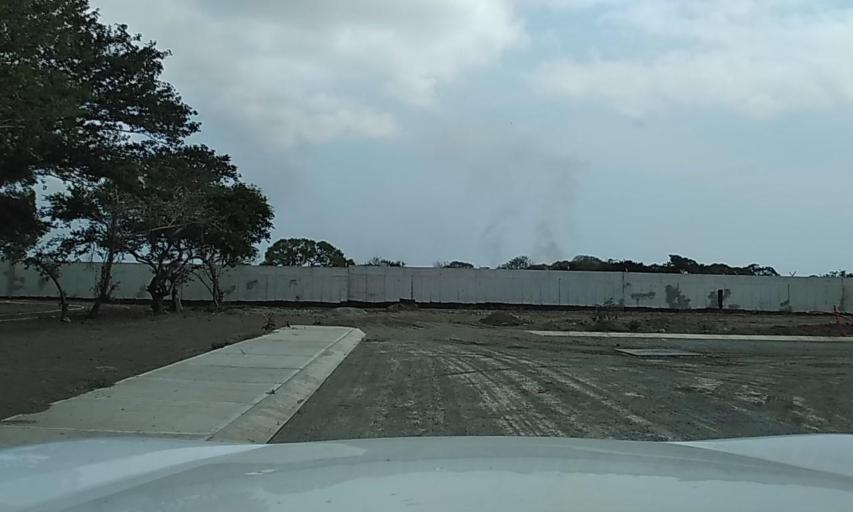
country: MX
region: Veracruz
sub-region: Veracruz
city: Las Amapolas
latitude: 19.1334
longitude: -96.2016
